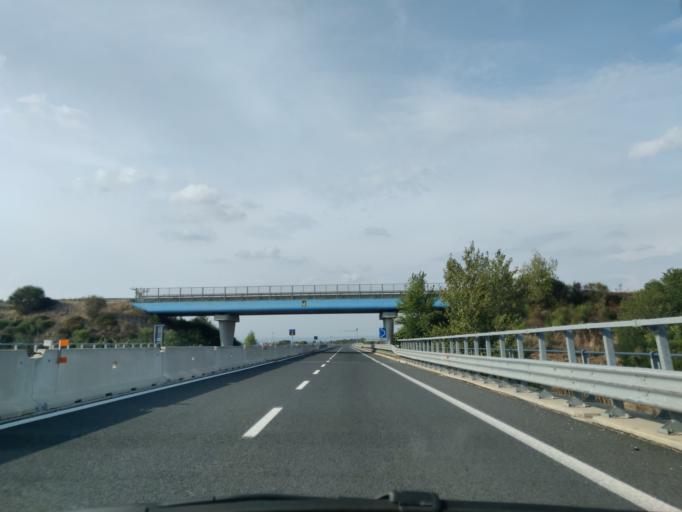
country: IT
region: Latium
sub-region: Provincia di Viterbo
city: Blera
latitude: 42.3437
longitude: 11.9823
